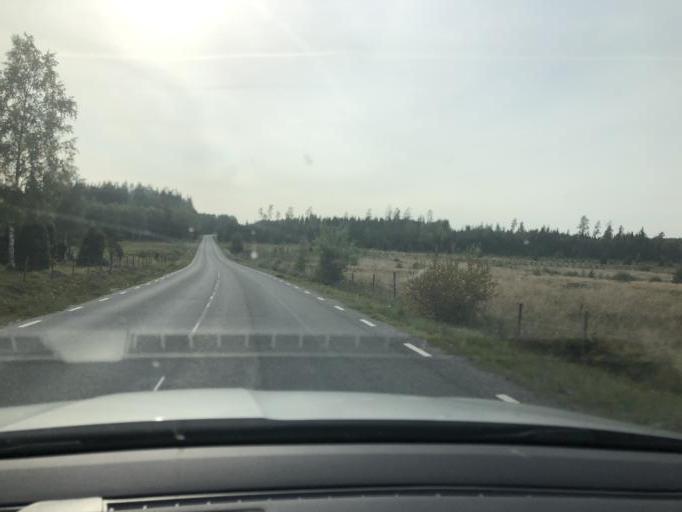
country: SE
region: Joenkoeping
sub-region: Vetlanda Kommun
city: Ekenassjon
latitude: 57.5277
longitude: 14.9316
